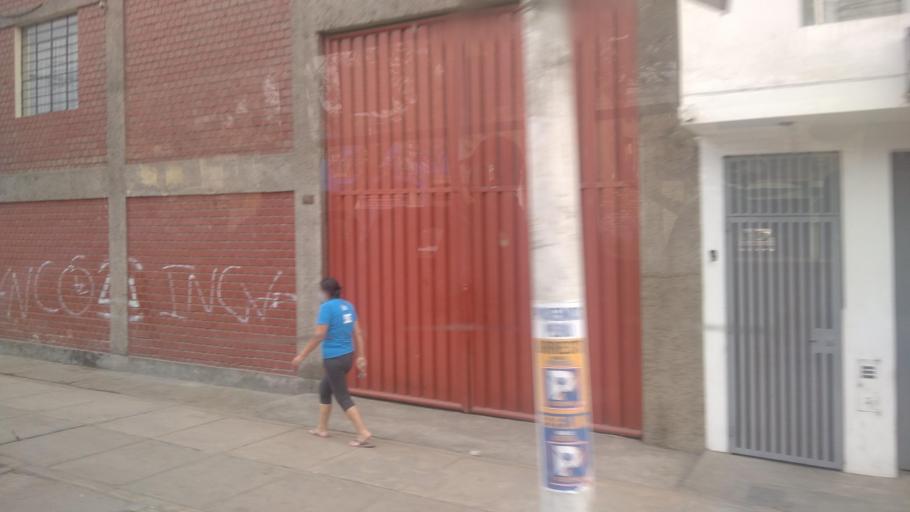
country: PE
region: Lima
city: Lima
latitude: -12.0052
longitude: -77.0022
